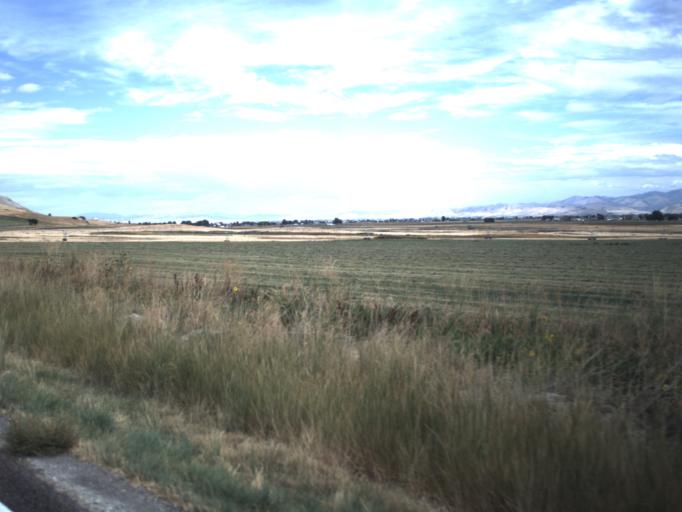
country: US
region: Utah
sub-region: Cache County
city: Benson
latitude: 41.8786
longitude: -111.9502
